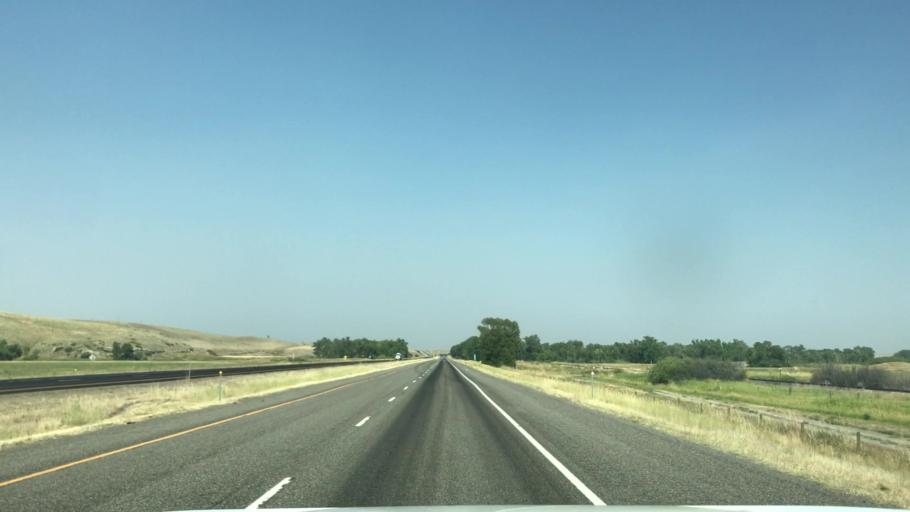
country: US
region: Montana
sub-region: Cascade County
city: Sun Prairie
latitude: 47.2318
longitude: -111.7530
